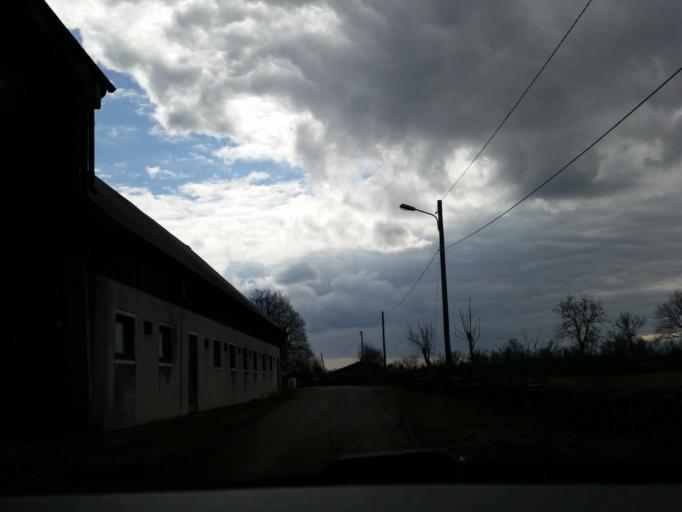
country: SE
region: Kalmar
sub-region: Morbylanga Kommun
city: Sodra Sandby
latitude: 56.6846
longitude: 16.5807
